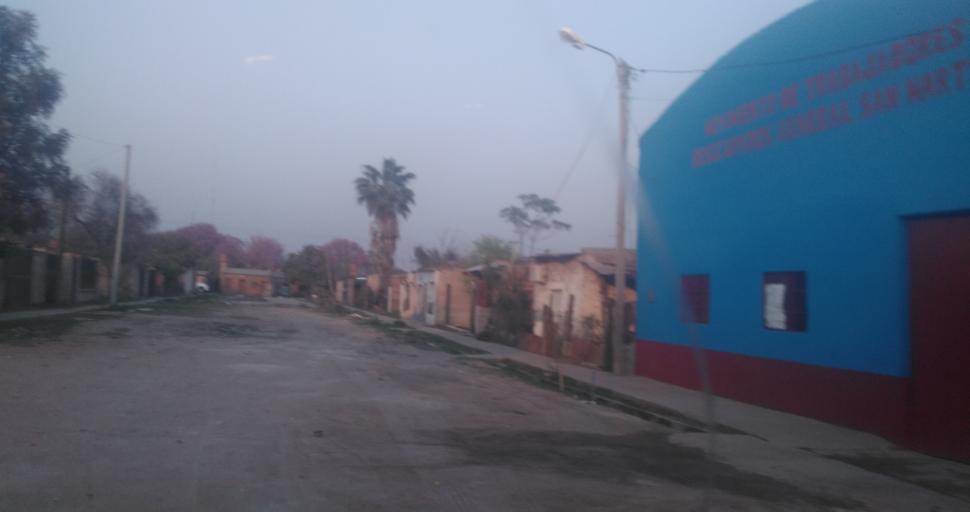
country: AR
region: Chaco
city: Resistencia
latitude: -27.4724
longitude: -59.0093
